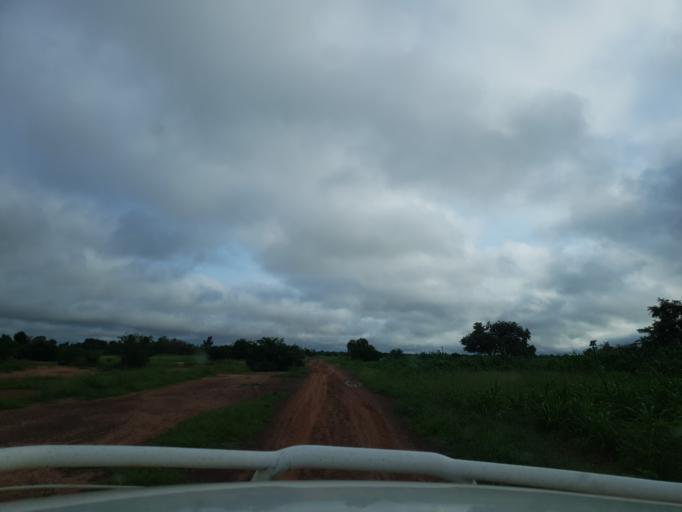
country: ML
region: Segou
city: Baroueli
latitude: 13.4061
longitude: -7.0061
